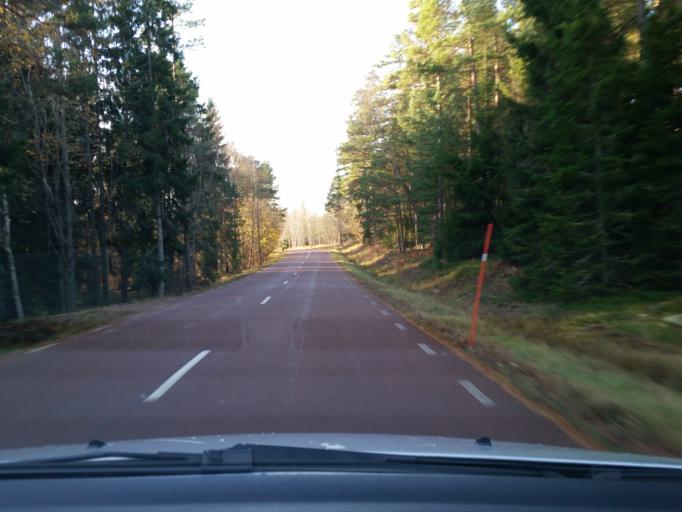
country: AX
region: Alands landsbygd
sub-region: Sund
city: Sund
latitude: 60.3082
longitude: 20.1897
